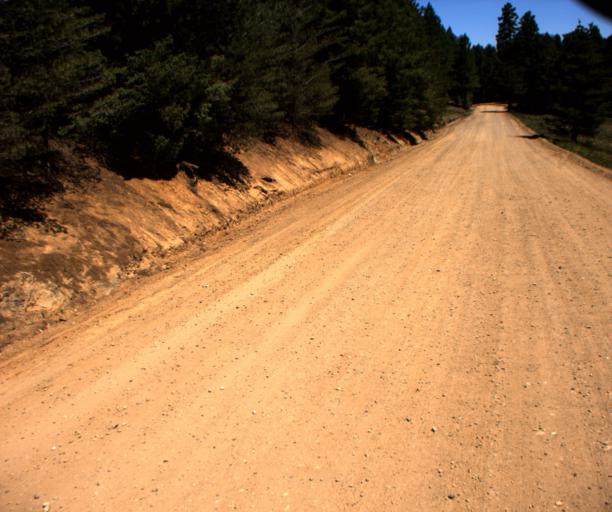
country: US
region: Arizona
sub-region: Graham County
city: Swift Trail Junction
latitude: 32.6687
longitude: -109.8773
